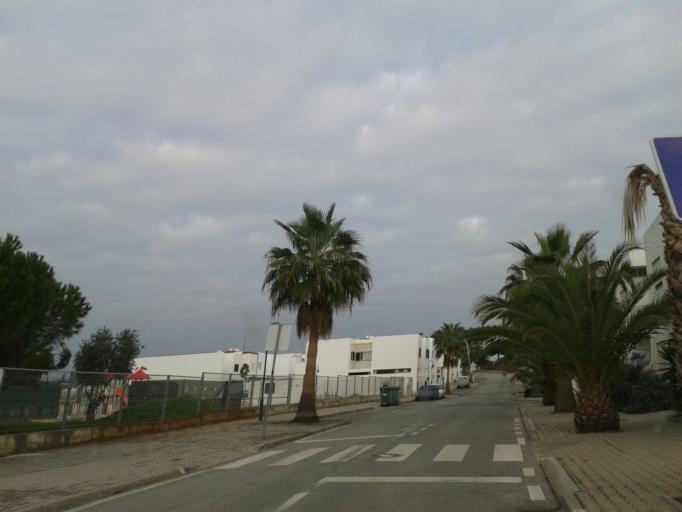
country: PT
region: Faro
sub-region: Castro Marim
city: Castro Marim
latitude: 37.2210
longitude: -7.4477
